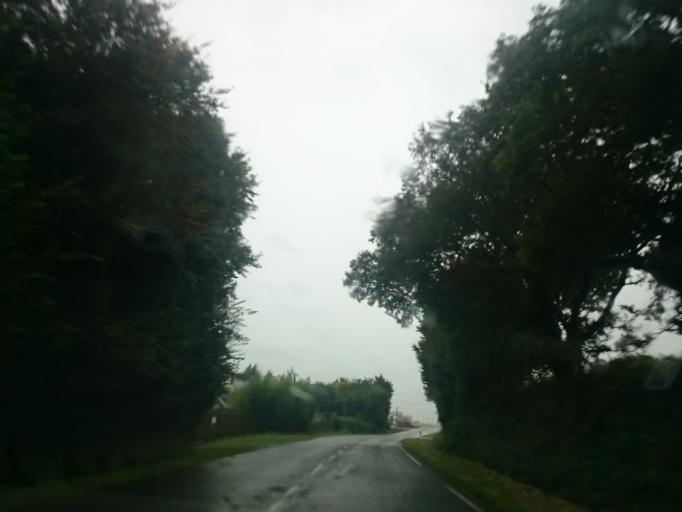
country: FR
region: Brittany
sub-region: Departement du Finistere
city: Plabennec
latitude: 48.5140
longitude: -4.4087
